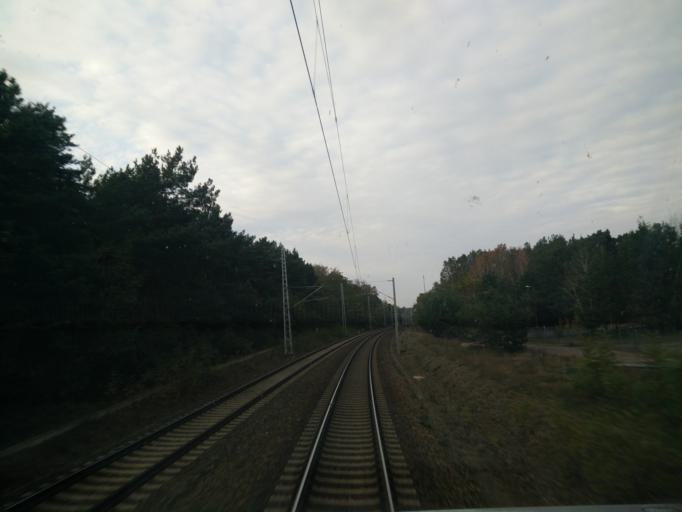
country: DE
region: Brandenburg
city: Gross Koris
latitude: 52.1618
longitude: 13.6497
